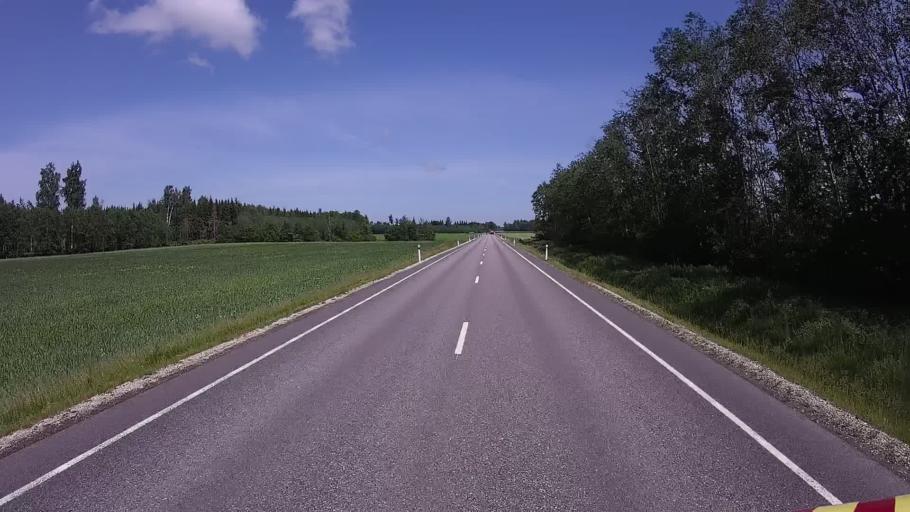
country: EE
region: Tartu
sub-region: Tartu linn
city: Tartu
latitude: 58.3823
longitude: 26.8870
